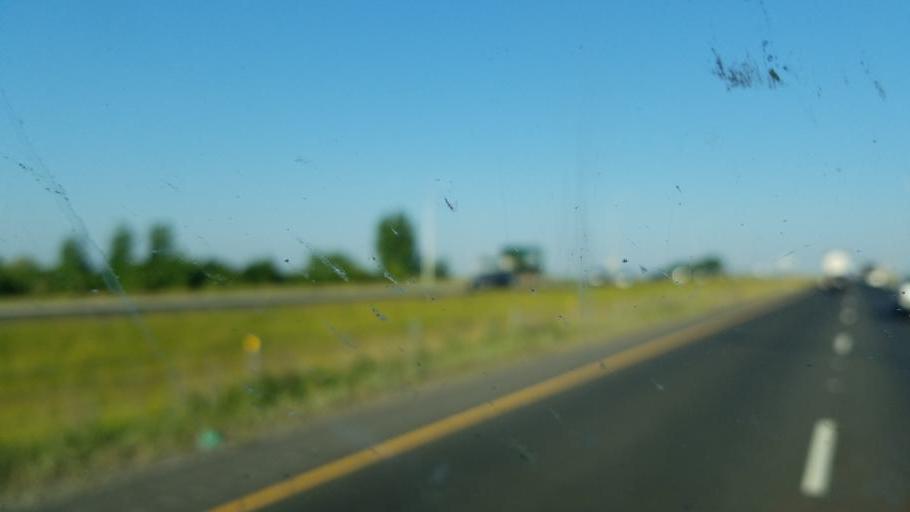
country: US
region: Illinois
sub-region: Will County
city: Shorewood
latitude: 41.4866
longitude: -88.1912
